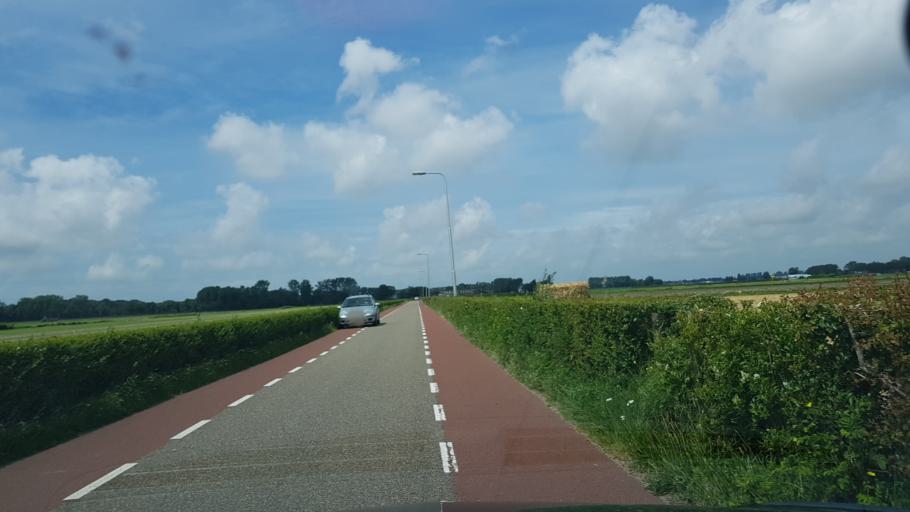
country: NL
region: South Holland
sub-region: Gemeente Lisse
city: Lisse
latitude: 52.2748
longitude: 4.5597
